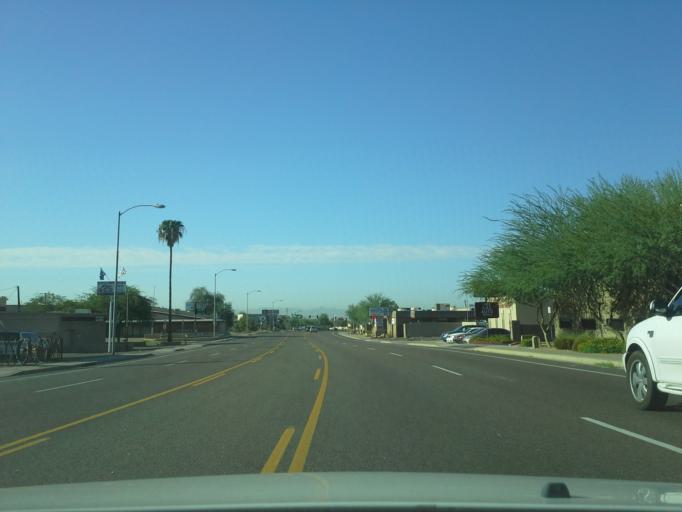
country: US
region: Arizona
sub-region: Maricopa County
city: Paradise Valley
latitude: 33.5847
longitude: -112.0503
